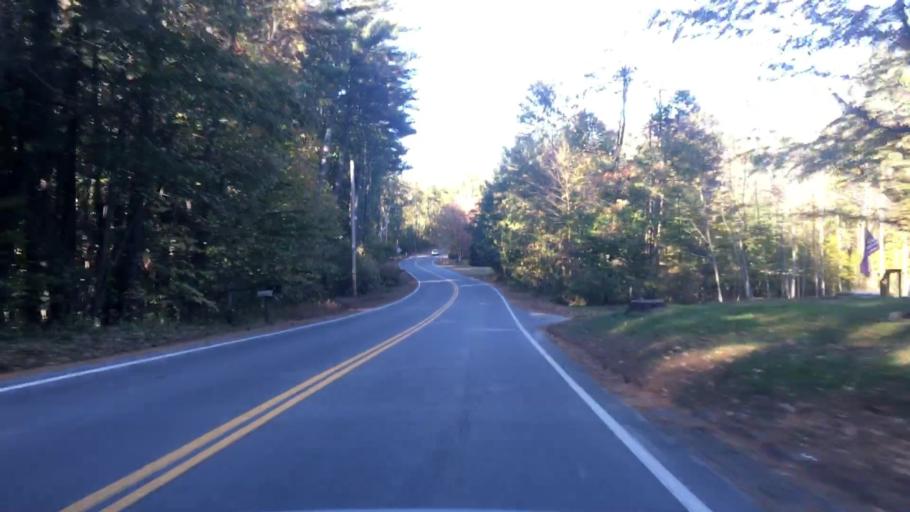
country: US
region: New Hampshire
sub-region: Merrimack County
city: Contoocook
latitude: 43.2578
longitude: -71.7343
